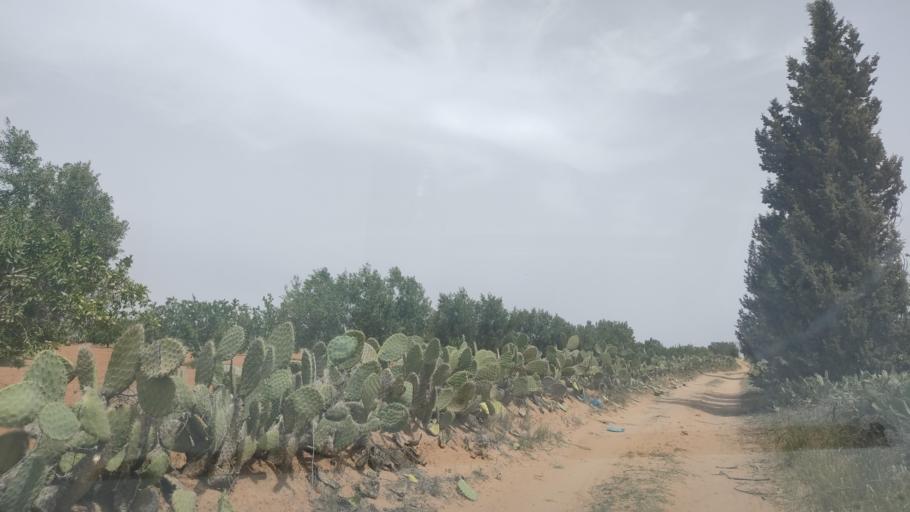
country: TN
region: Safaqis
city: Sfax
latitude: 34.8439
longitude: 10.5912
